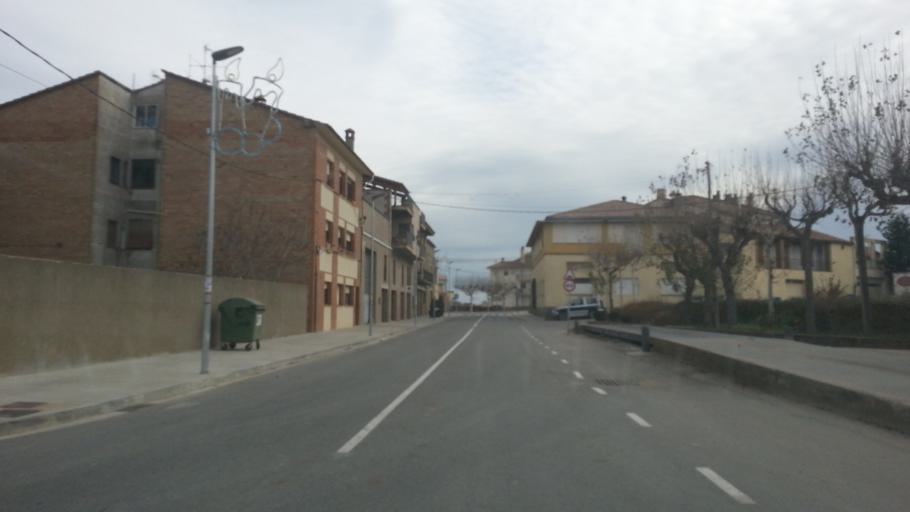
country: ES
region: Catalonia
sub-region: Provincia de Barcelona
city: Capolat
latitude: 42.0180
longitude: 1.7338
